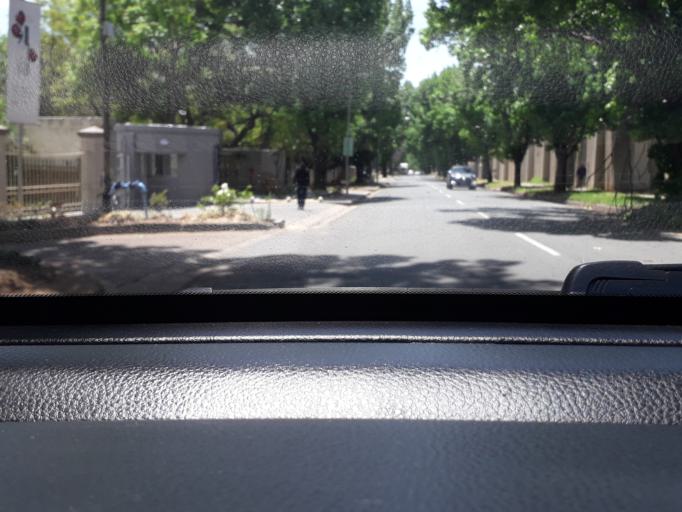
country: ZA
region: Gauteng
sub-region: City of Johannesburg Metropolitan Municipality
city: Johannesburg
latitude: -26.1336
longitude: 28.0716
